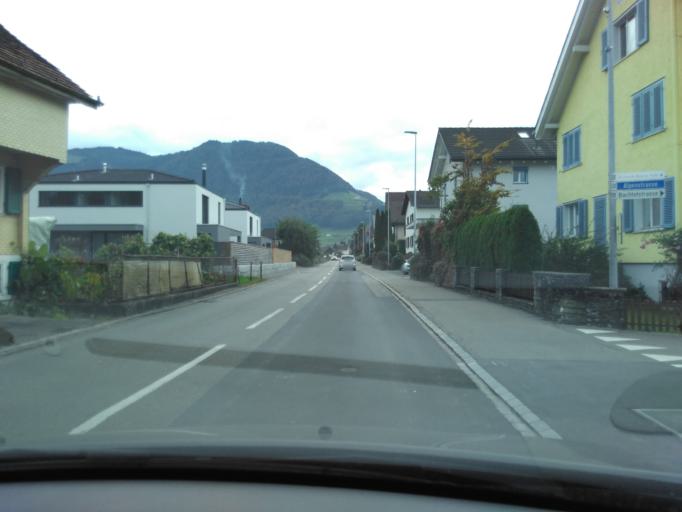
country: CH
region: Schwyz
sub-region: Bezirk March
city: Schubelbach
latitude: 47.1882
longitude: 8.8972
